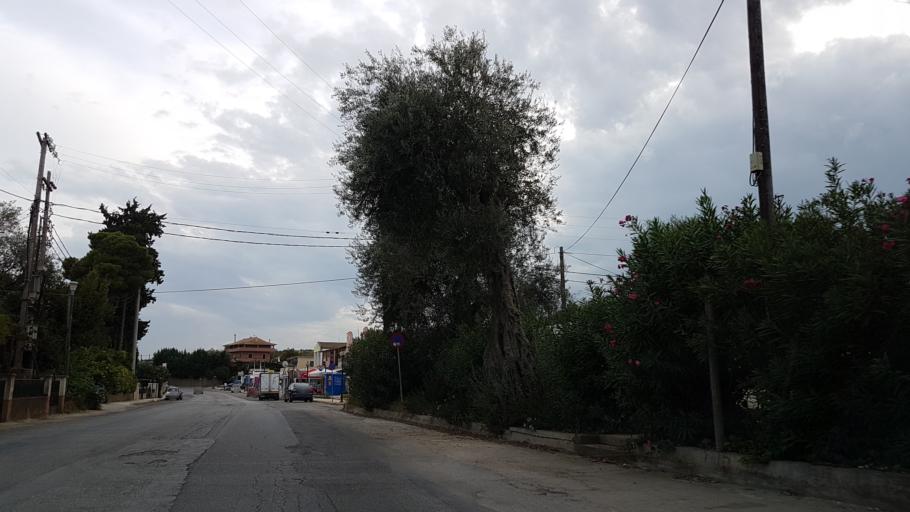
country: GR
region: Ionian Islands
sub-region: Nomos Kerkyras
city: Kontokali
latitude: 39.6751
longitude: 19.8394
